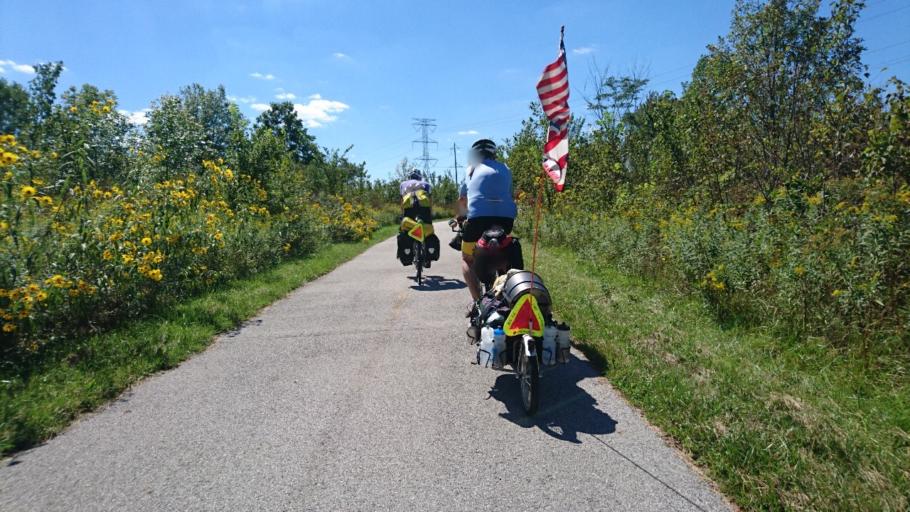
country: US
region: Illinois
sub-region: Cook County
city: Lansing
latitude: 41.5462
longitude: -87.5669
